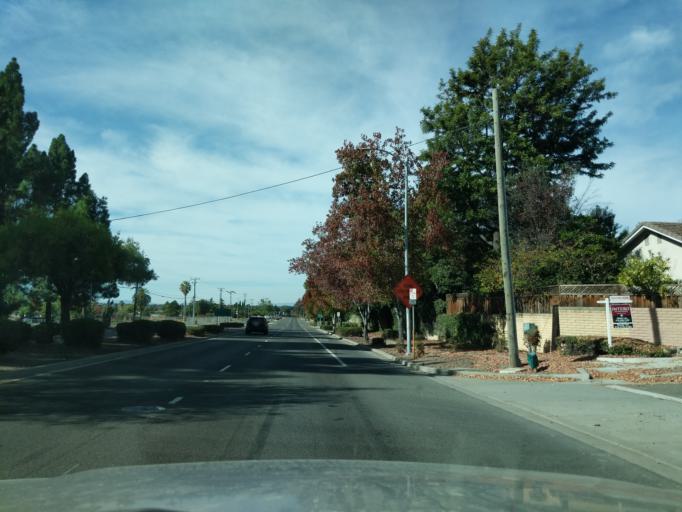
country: US
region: California
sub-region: Alameda County
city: Fremont
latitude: 37.5460
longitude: -121.9333
